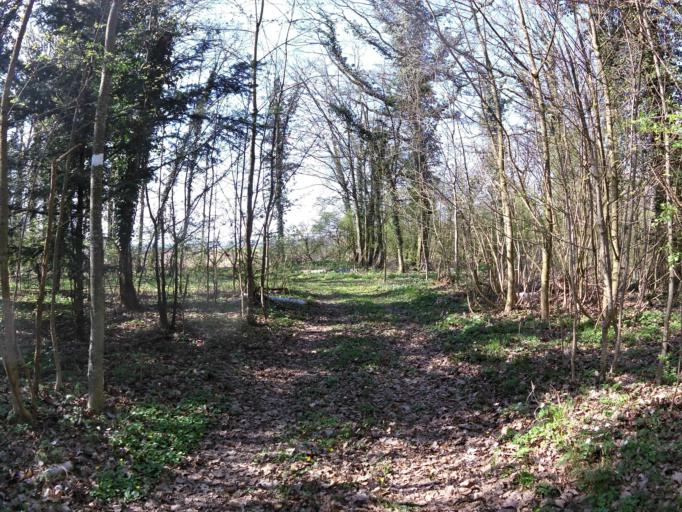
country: DE
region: Bavaria
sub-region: Regierungsbezirk Unterfranken
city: Kurnach
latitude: 49.8279
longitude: 10.0555
